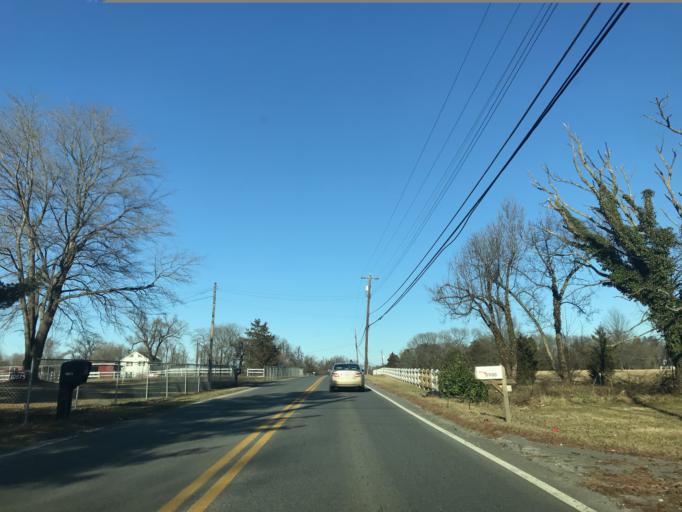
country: US
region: Maryland
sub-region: Prince George's County
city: Friendly
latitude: 38.7403
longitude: -76.9398
